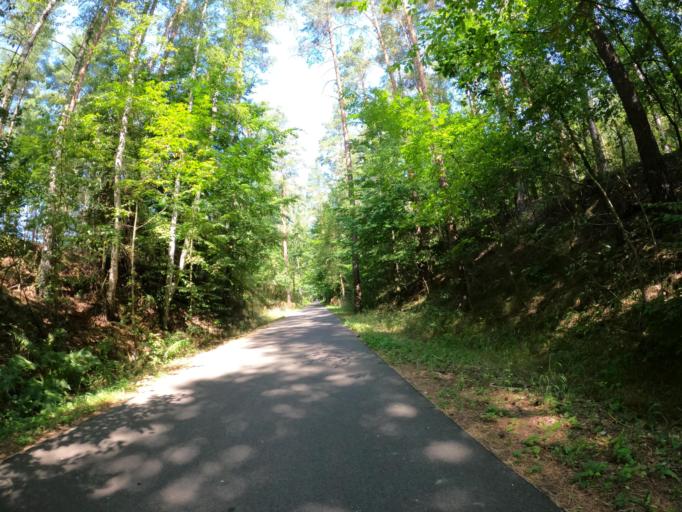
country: DE
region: Brandenburg
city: Templin
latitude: 53.1670
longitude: 13.5202
